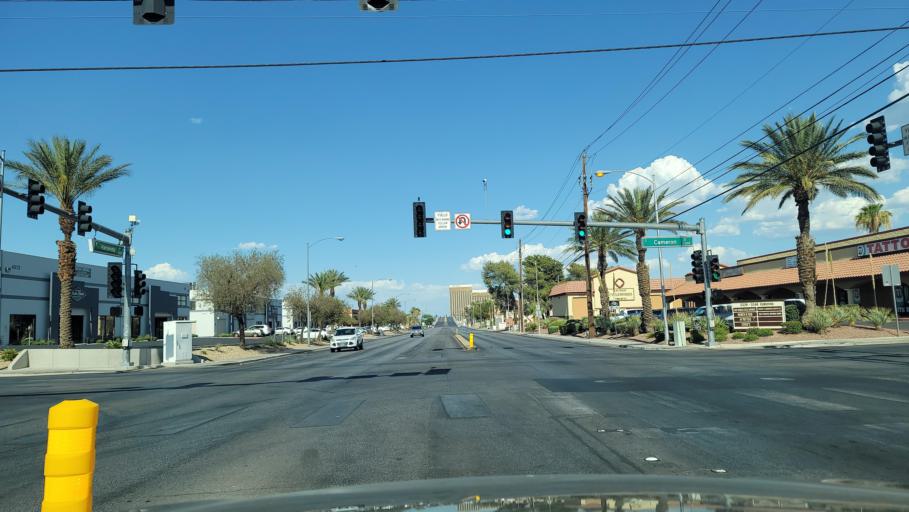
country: US
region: Nevada
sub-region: Clark County
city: Spring Valley
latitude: 36.0936
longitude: -115.2041
